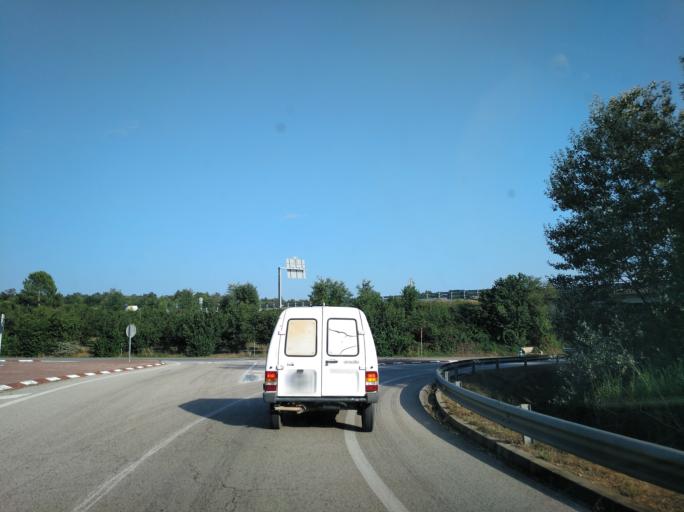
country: ES
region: Catalonia
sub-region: Provincia de Girona
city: Brunyola
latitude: 41.8791
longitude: 2.6958
